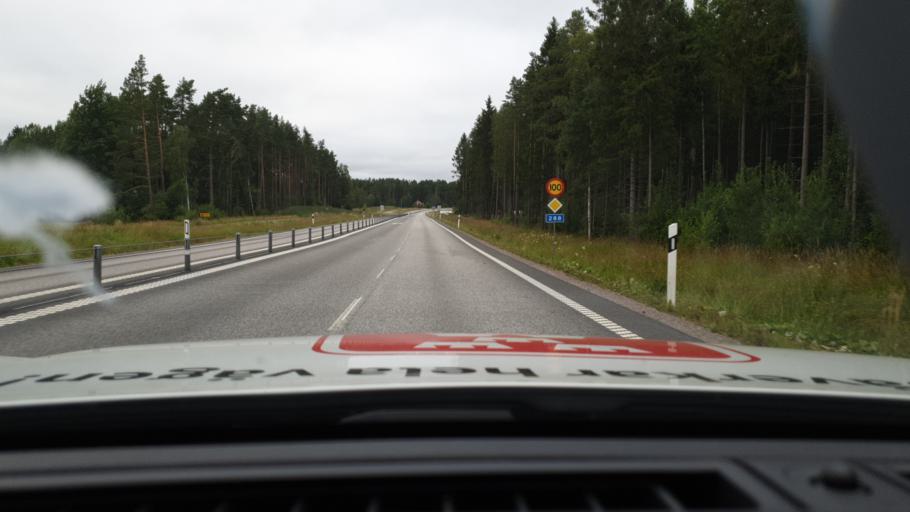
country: SE
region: Uppsala
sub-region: Osthammars Kommun
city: Gimo
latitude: 60.1013
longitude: 18.1256
